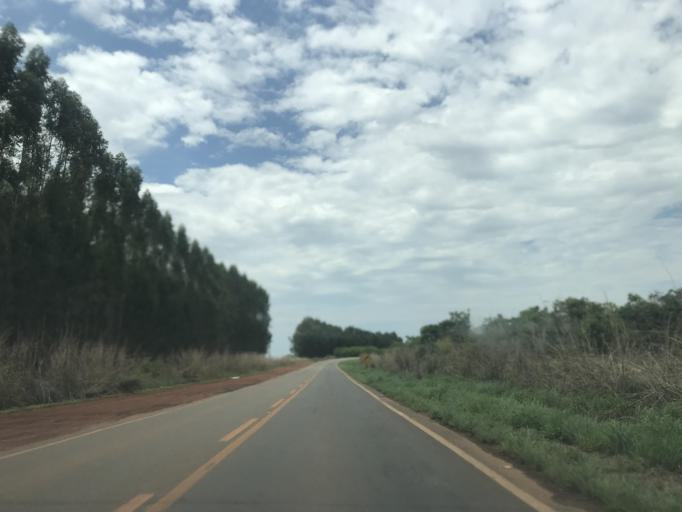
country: BR
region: Goias
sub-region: Luziania
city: Luziania
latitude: -16.3411
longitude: -48.0186
